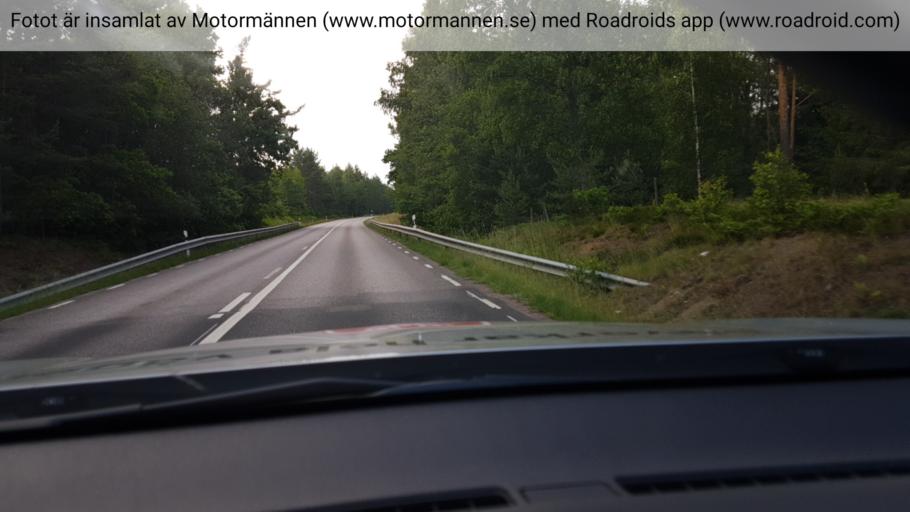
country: SE
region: Vaestra Goetaland
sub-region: Hjo Kommun
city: Hjo
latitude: 58.1698
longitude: 14.2068
